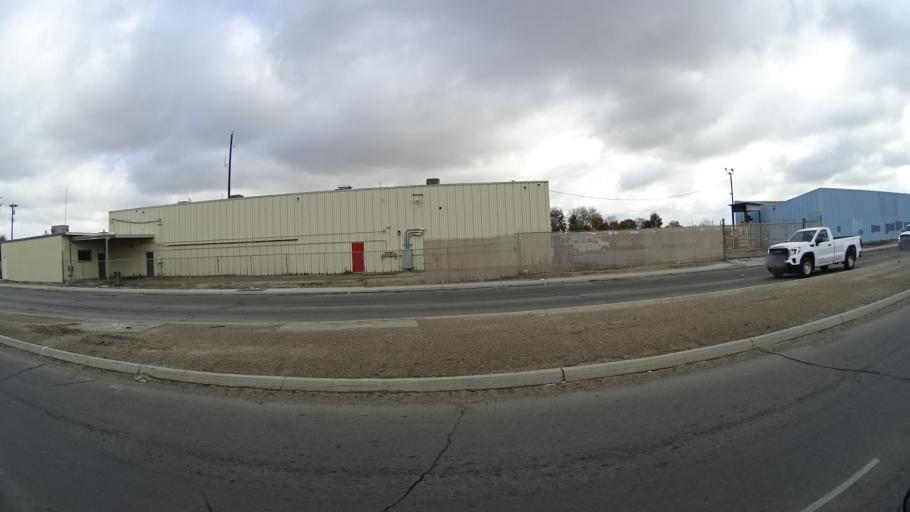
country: US
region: California
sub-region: Kern County
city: Bakersfield
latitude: 35.3497
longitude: -118.9855
